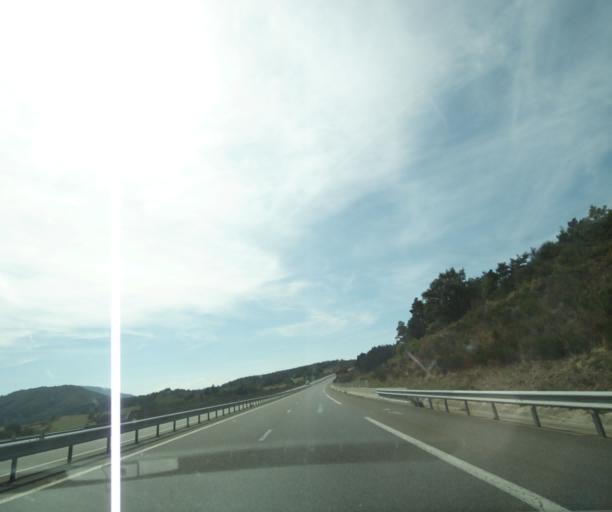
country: FR
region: Auvergne
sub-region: Departement du Puy-de-Dome
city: Charbonnieres-les-Varennes
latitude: 45.9108
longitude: 2.9546
